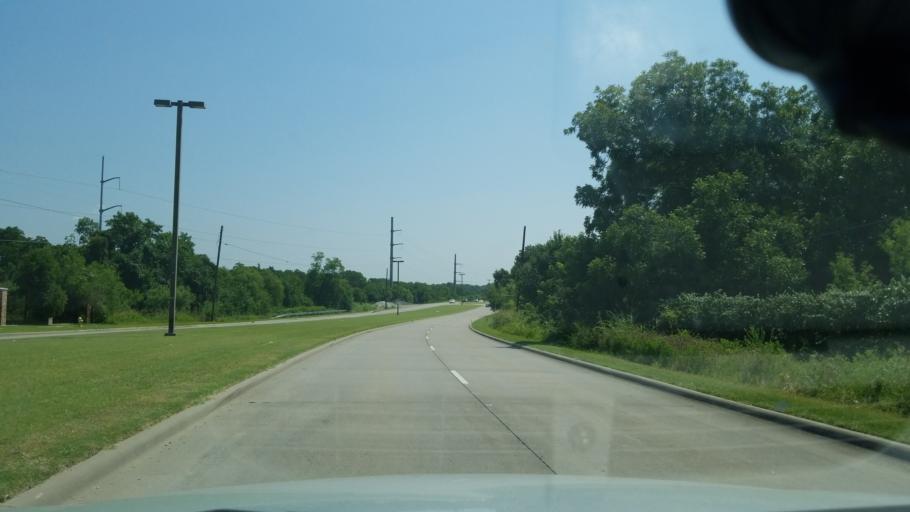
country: US
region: Texas
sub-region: Dallas County
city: Coppell
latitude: 32.9526
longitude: -96.9824
